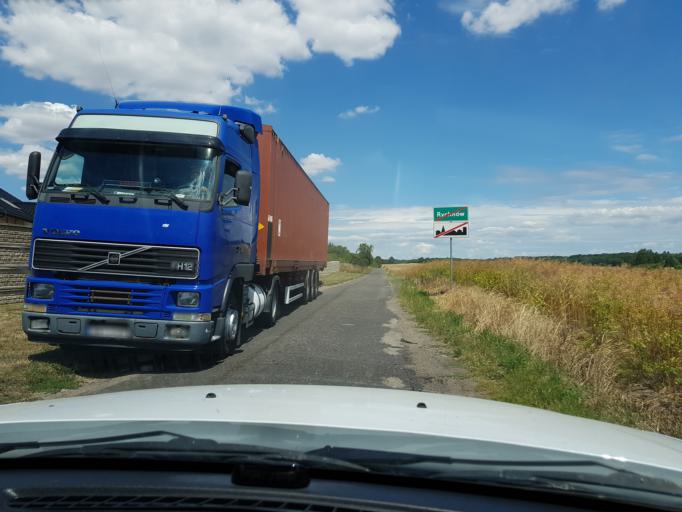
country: PL
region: West Pomeranian Voivodeship
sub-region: Powiat mysliborski
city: Barlinek
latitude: 52.9635
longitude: 15.1224
